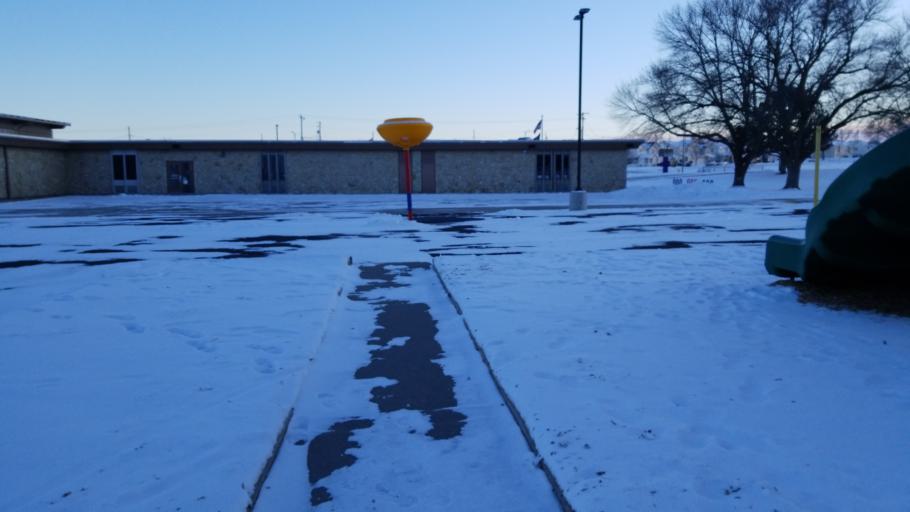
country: US
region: Nebraska
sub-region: Sarpy County
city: Offutt Air Force Base
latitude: 41.1304
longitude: -95.9522
